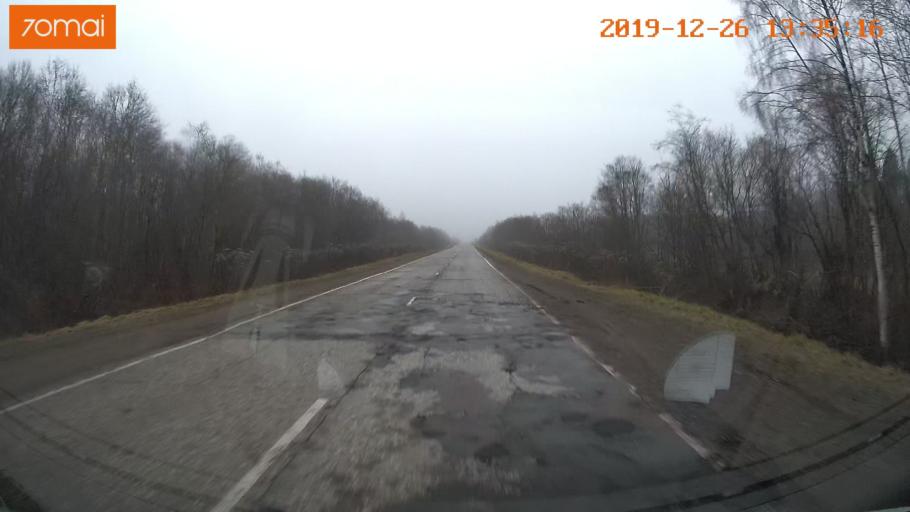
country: RU
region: Vologda
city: Sheksna
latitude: 58.7957
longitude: 38.3372
